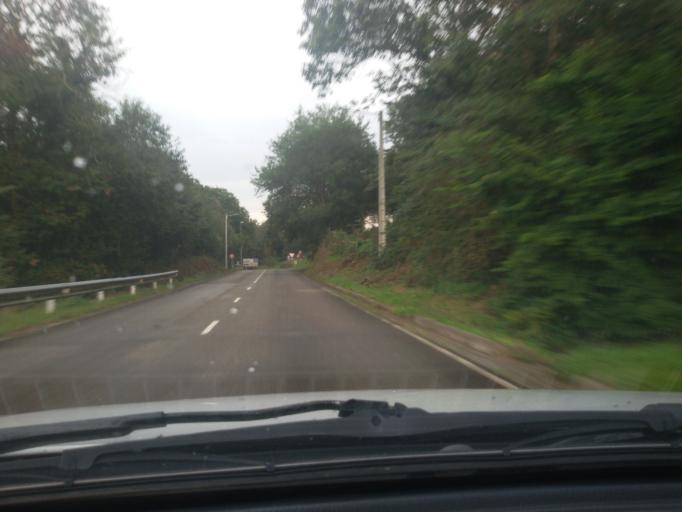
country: ES
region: Asturias
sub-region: Province of Asturias
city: Norena
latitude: 43.3722
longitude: -5.7304
